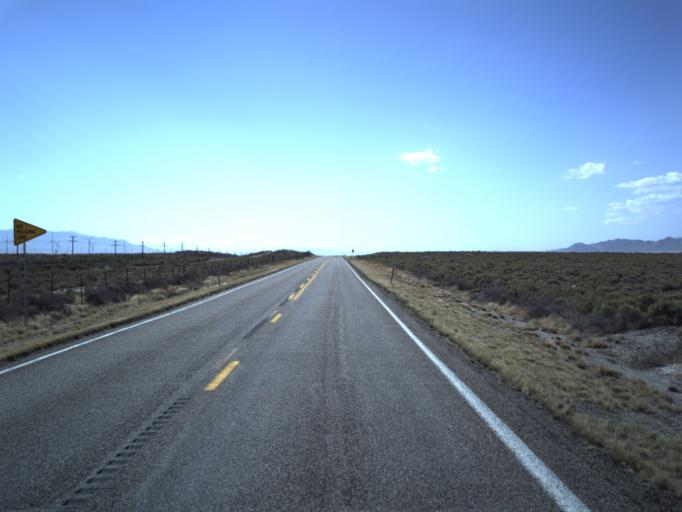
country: US
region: Utah
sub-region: Beaver County
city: Milford
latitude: 38.6287
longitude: -112.9844
